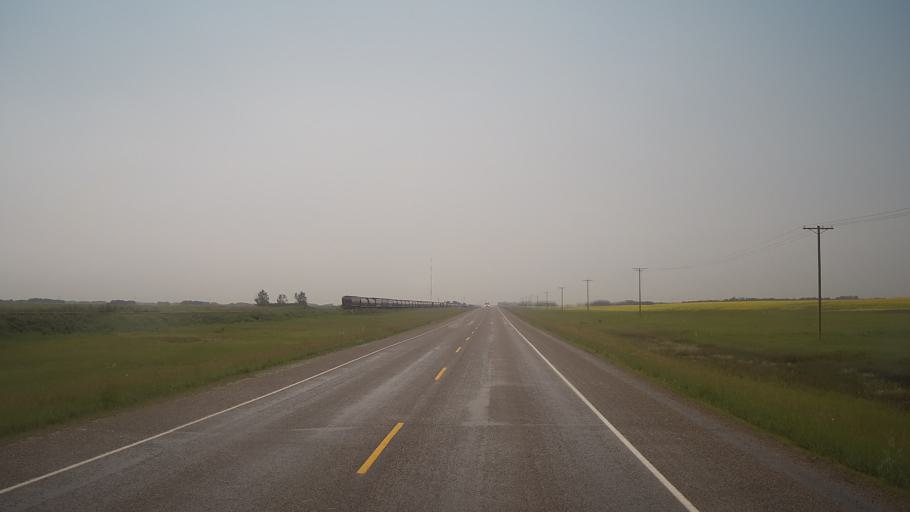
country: CA
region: Saskatchewan
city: Biggar
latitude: 52.1651
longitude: -108.2998
